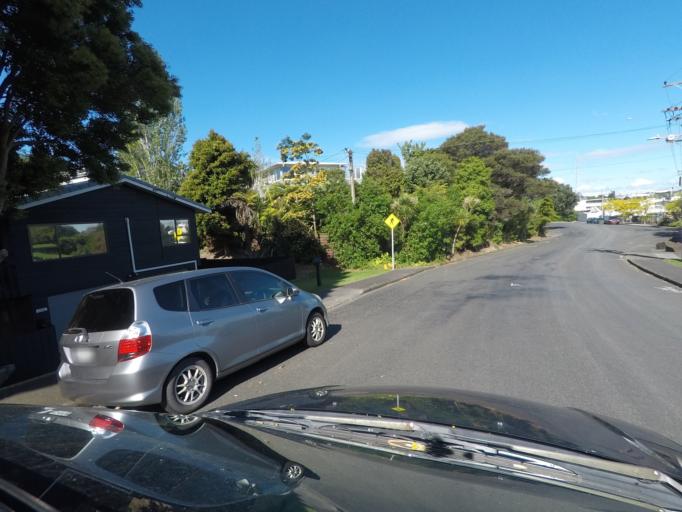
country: NZ
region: Auckland
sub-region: Auckland
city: Rosebank
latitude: -36.8604
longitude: 174.6552
